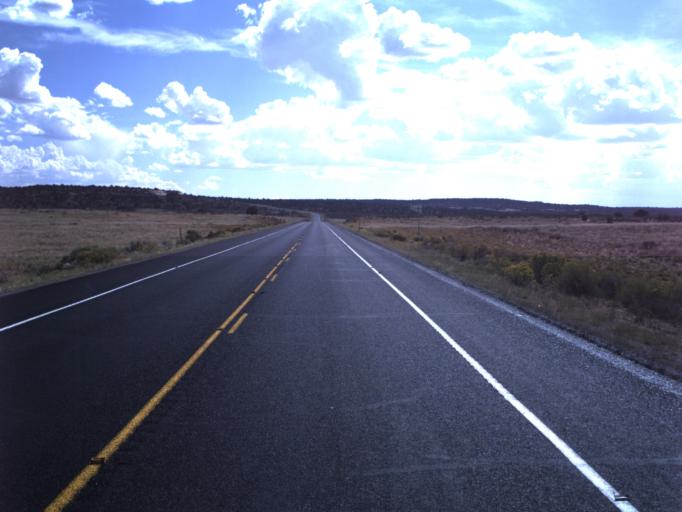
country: US
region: Utah
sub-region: Grand County
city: Moab
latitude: 38.6248
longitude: -109.8098
